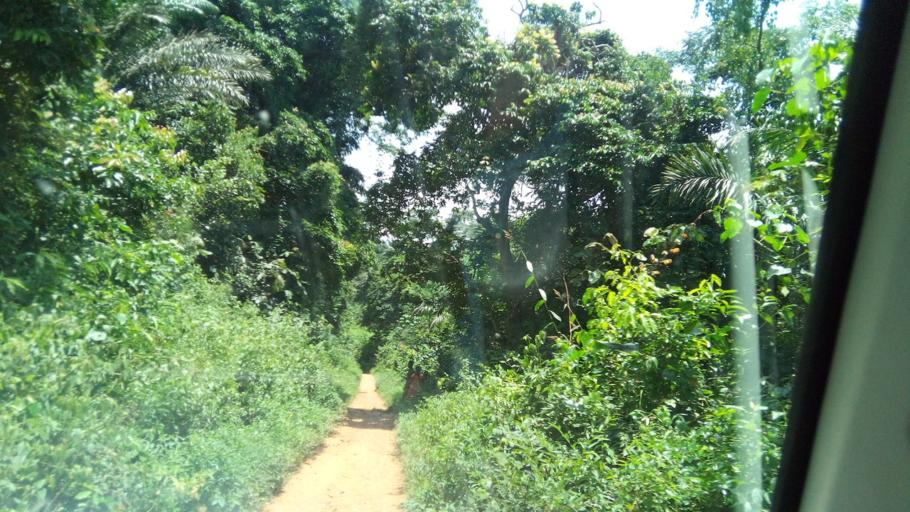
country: AO
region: Zaire
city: Mbanza Congo
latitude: -5.8104
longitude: 14.2449
